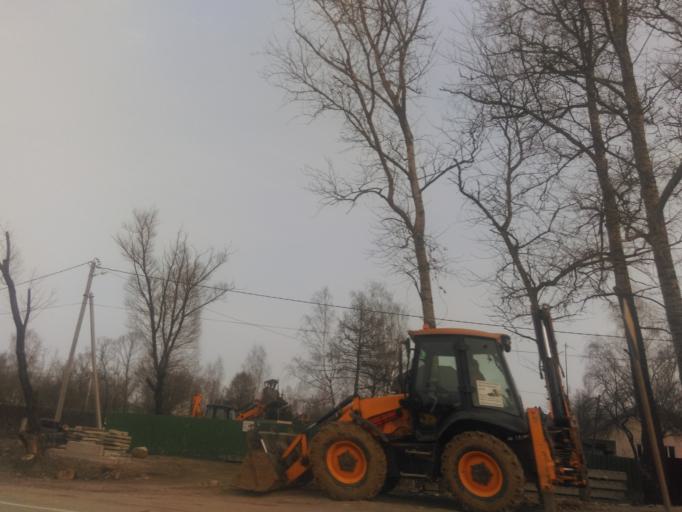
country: RU
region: Moskovskaya
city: Chupryakovo
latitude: 55.5597
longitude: 36.5639
